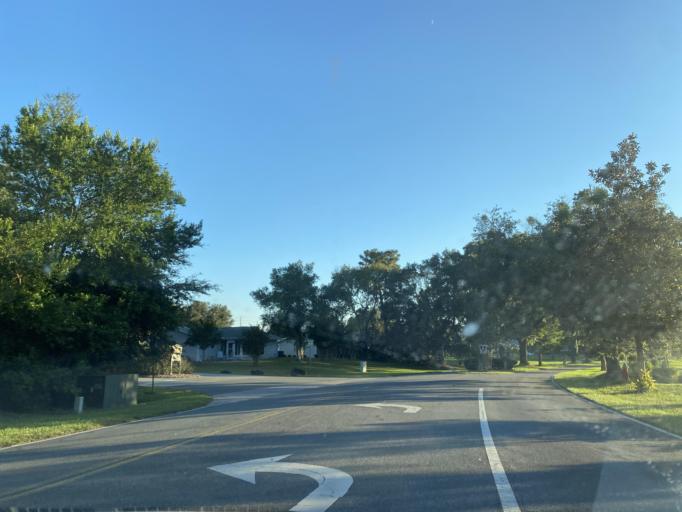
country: US
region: Florida
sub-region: Marion County
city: Ocala
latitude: 29.0554
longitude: -82.2588
